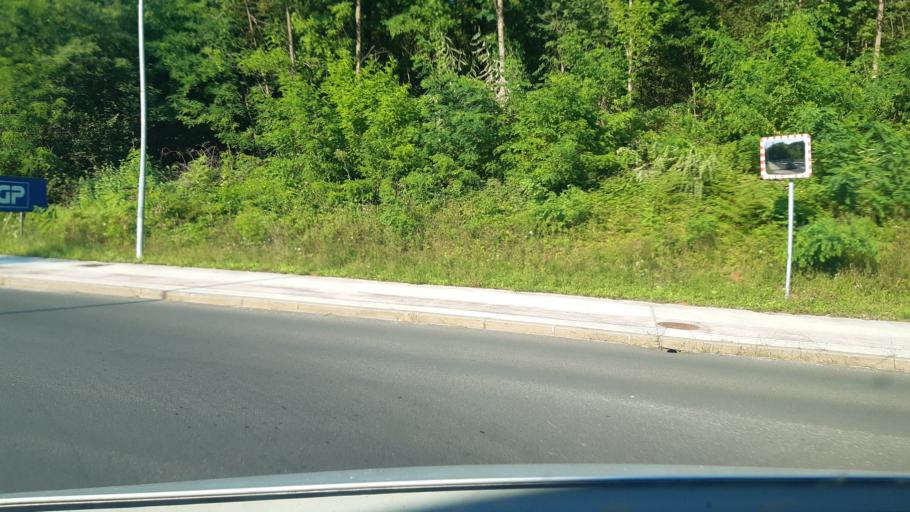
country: SI
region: Crnomelj
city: Crnomelj
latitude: 45.5835
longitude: 15.1839
